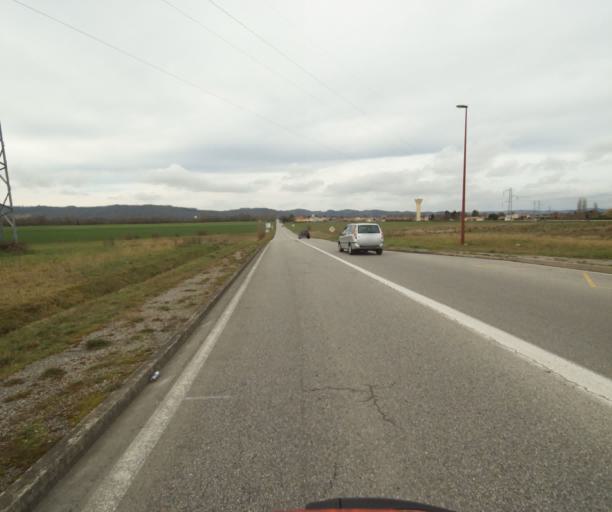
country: FR
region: Midi-Pyrenees
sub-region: Departement de l'Ariege
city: La Tour-du-Crieu
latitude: 43.0979
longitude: 1.6537
